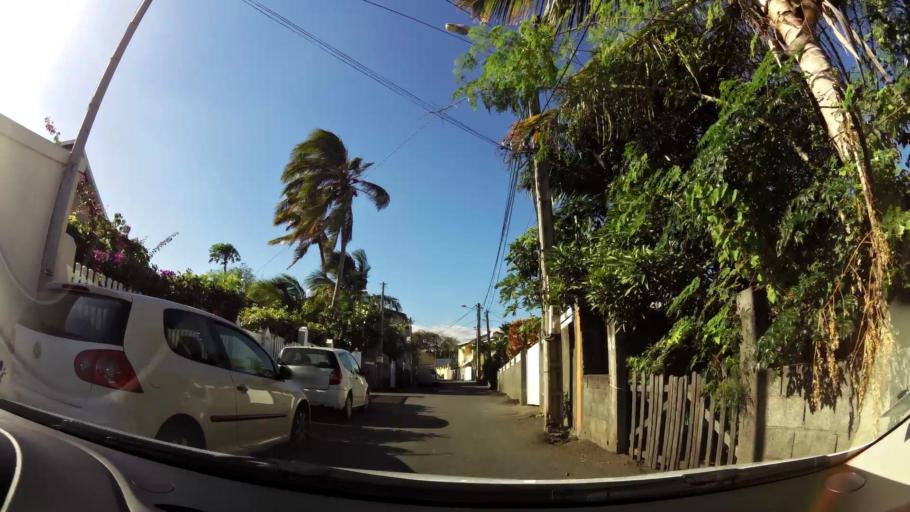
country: RE
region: Reunion
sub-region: Reunion
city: Saint-Pierre
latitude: -21.3457
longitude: 55.4824
